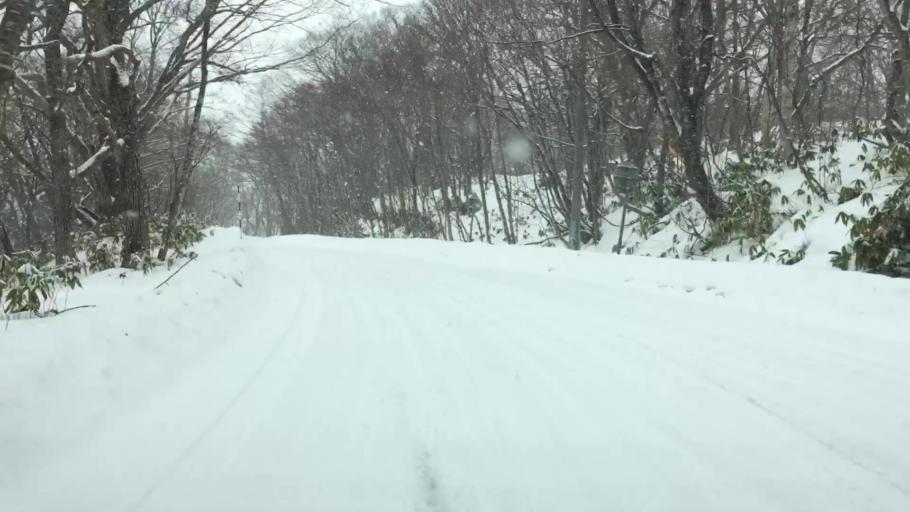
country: JP
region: Tochigi
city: Nikko
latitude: 36.9198
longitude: 139.7400
